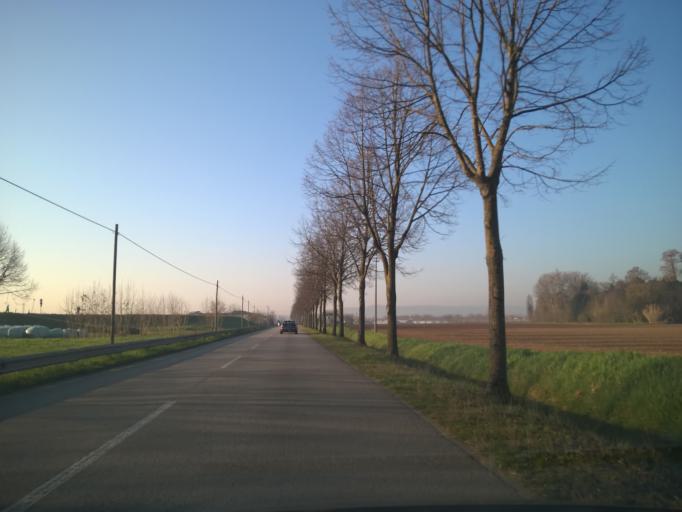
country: IT
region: Veneto
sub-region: Provincia di Vicenza
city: Quinto Vicentino
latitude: 45.5627
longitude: 11.6227
